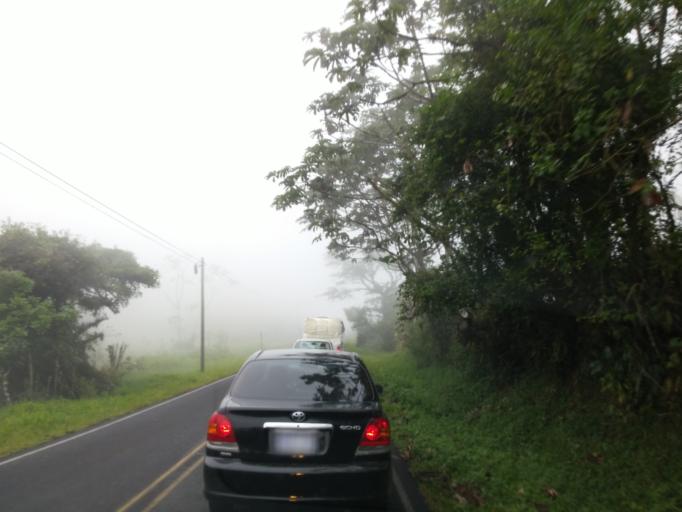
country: CR
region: Alajuela
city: San Ramon
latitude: 10.1782
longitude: -84.5016
